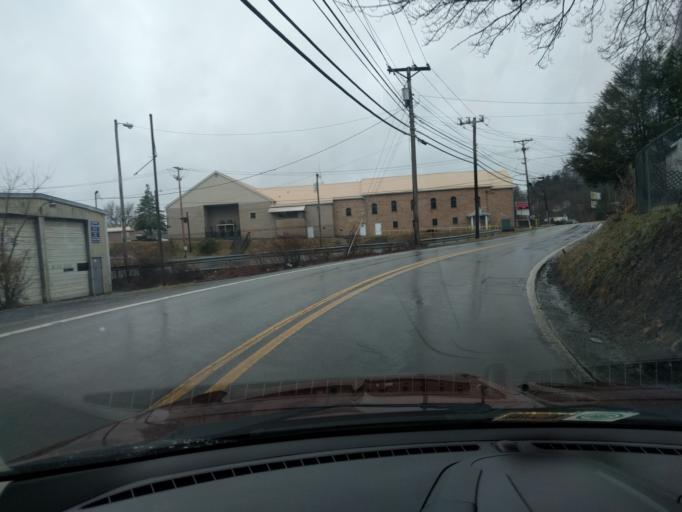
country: US
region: West Virginia
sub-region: Raleigh County
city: Beckley
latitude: 37.7927
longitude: -81.1819
